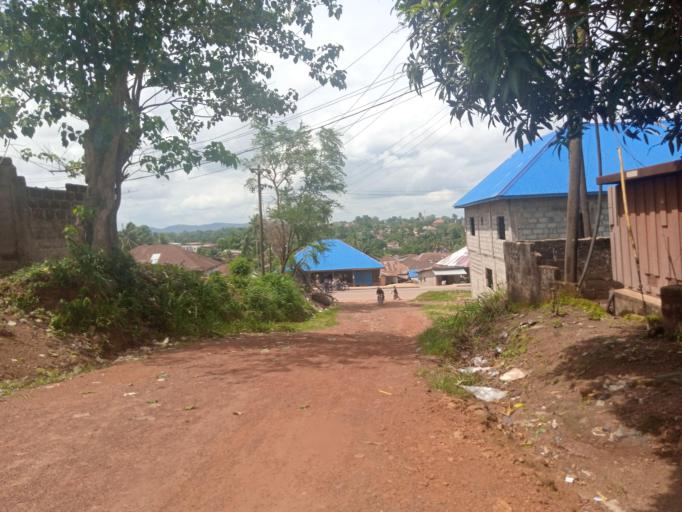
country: SL
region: Southern Province
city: Bo
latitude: 7.9681
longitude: -11.7335
